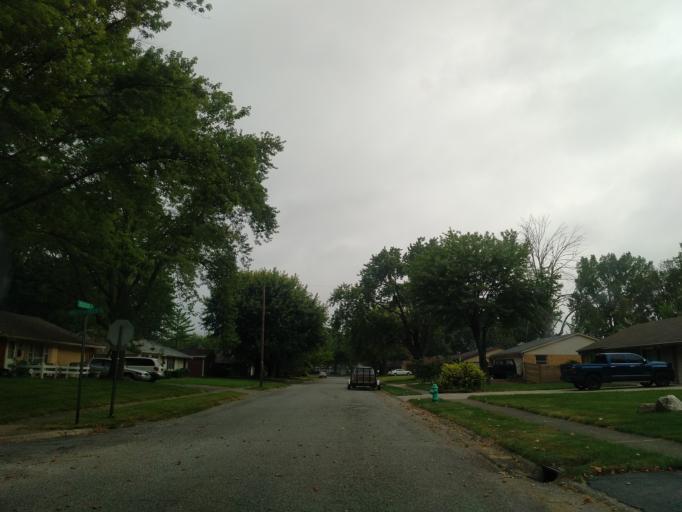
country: US
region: Indiana
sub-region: Marion County
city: Cumberland
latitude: 39.7936
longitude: -85.9816
